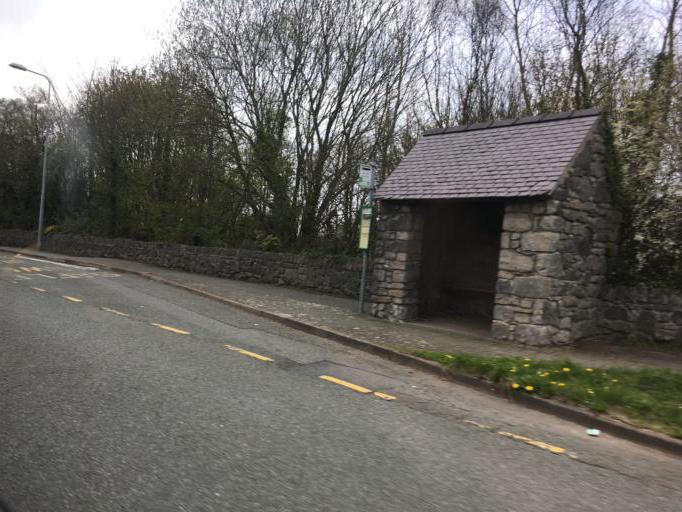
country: GB
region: Wales
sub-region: Gwynedd
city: Y Felinheli
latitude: 53.1783
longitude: -4.2182
